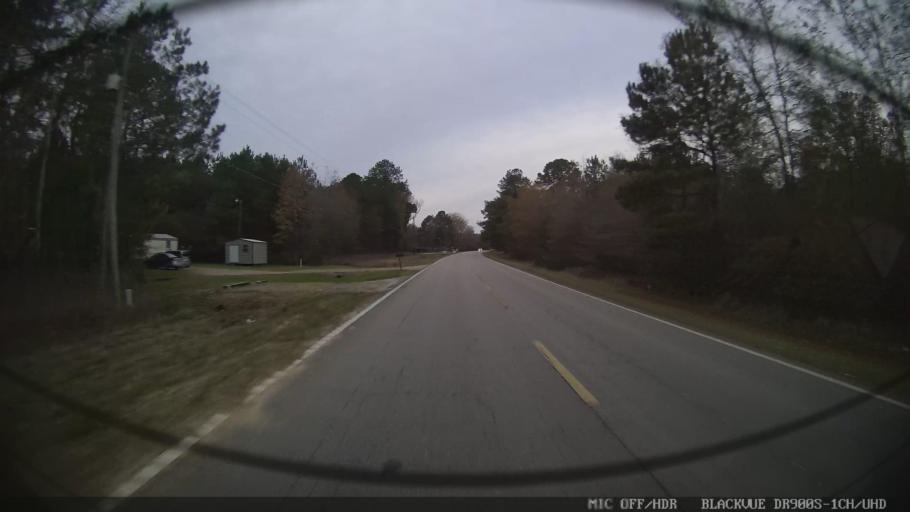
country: US
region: Mississippi
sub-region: Clarke County
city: Stonewall
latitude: 32.0276
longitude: -88.8617
